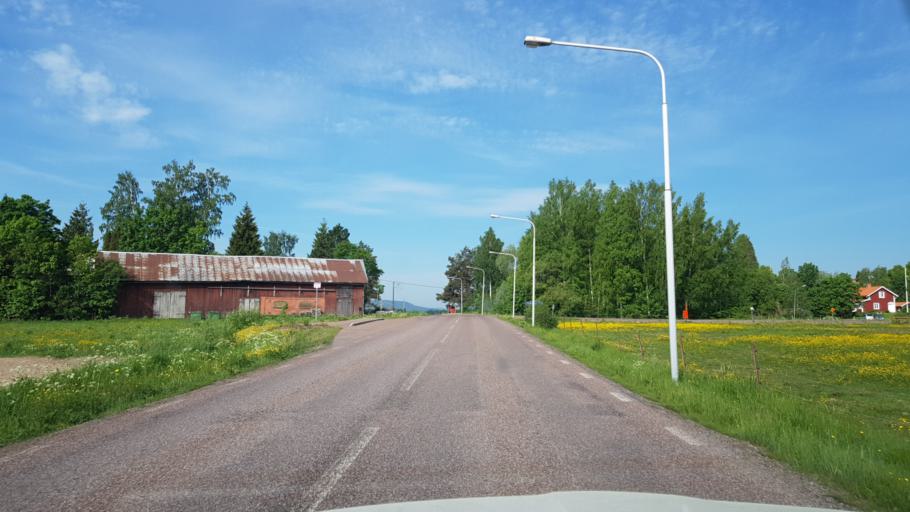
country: SE
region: Dalarna
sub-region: Borlange Kommun
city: Ornas
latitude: 60.4238
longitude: 15.6200
